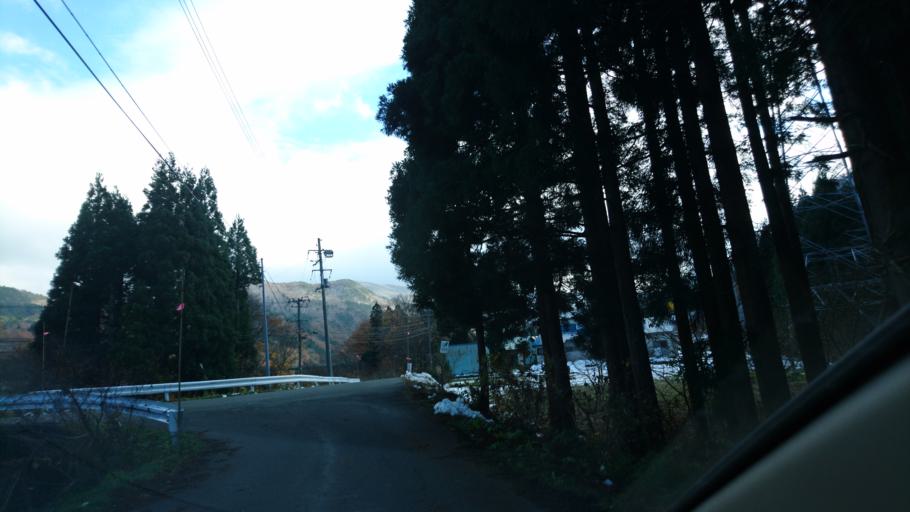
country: JP
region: Iwate
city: Kitakami
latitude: 39.2942
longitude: 140.8379
